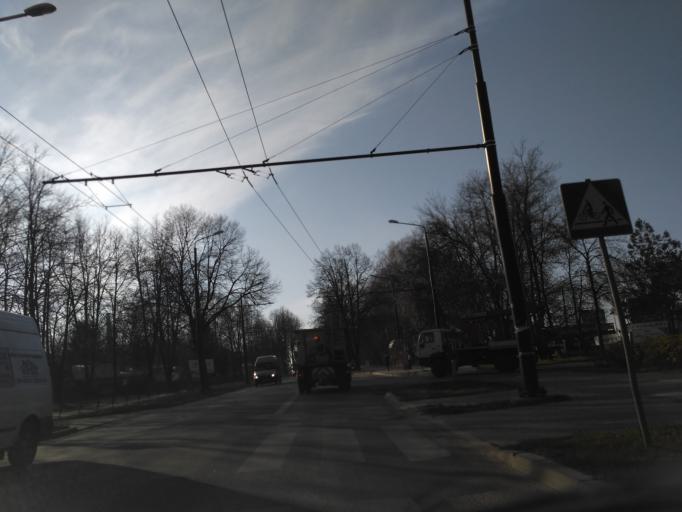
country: PL
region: Lublin Voivodeship
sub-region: Powiat lubelski
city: Lublin
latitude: 51.2083
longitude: 22.5691
